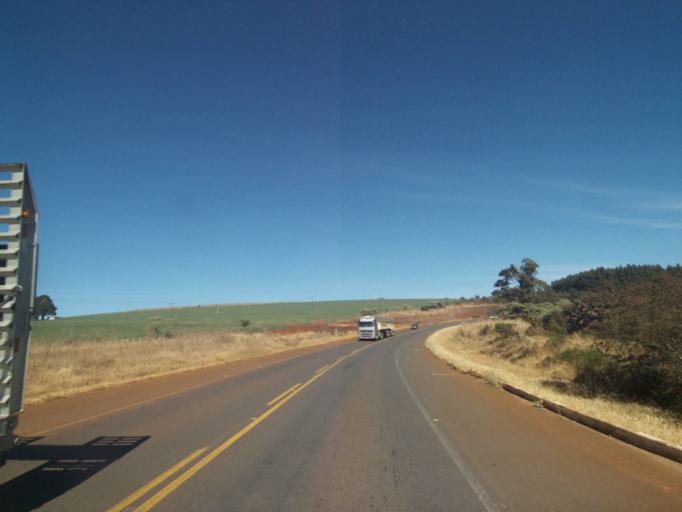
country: BR
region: Parana
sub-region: Tibagi
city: Tibagi
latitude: -24.7462
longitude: -50.4612
